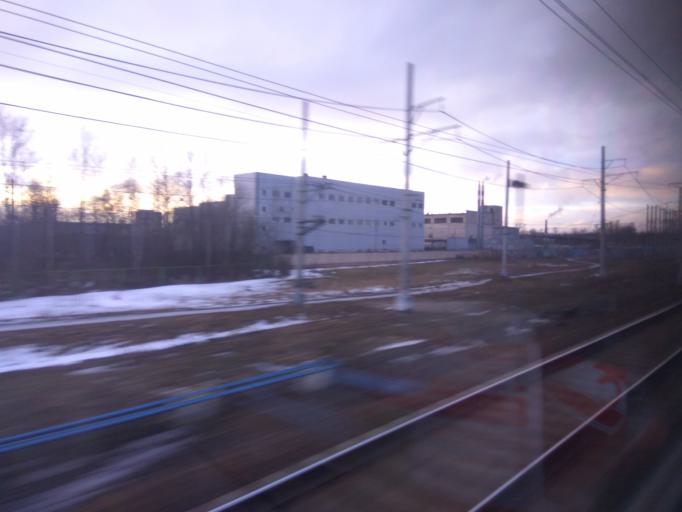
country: RU
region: St.-Petersburg
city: Centralniy
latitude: 59.8942
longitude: 30.3906
